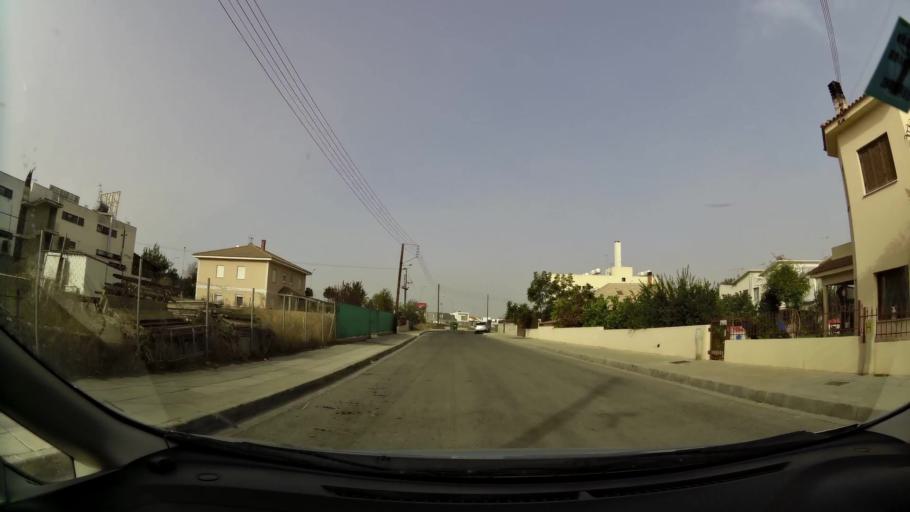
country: CY
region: Lefkosia
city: Geri
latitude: 35.0655
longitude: 33.3862
